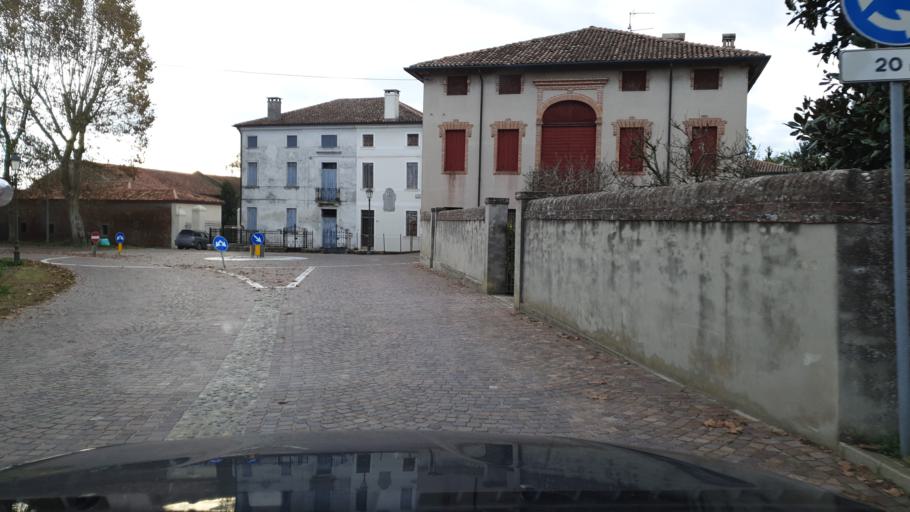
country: IT
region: Veneto
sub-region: Provincia di Rovigo
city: Fratta Polesine
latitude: 45.0299
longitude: 11.6401
